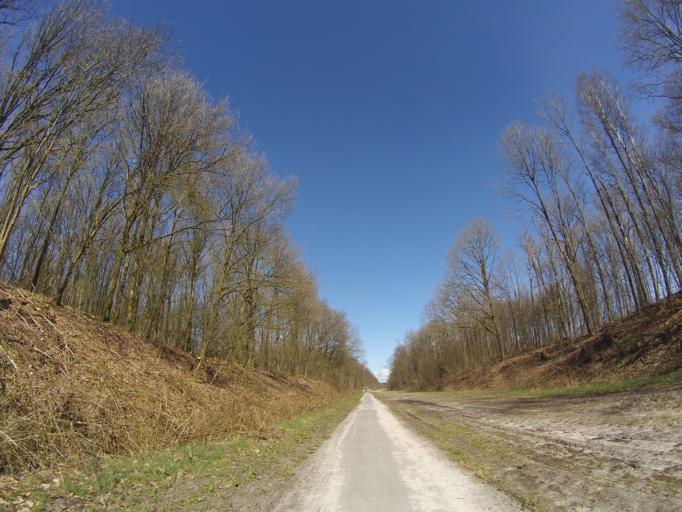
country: NL
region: Drenthe
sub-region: Gemeente Emmen
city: Klazienaveen
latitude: 52.7668
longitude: 6.9826
